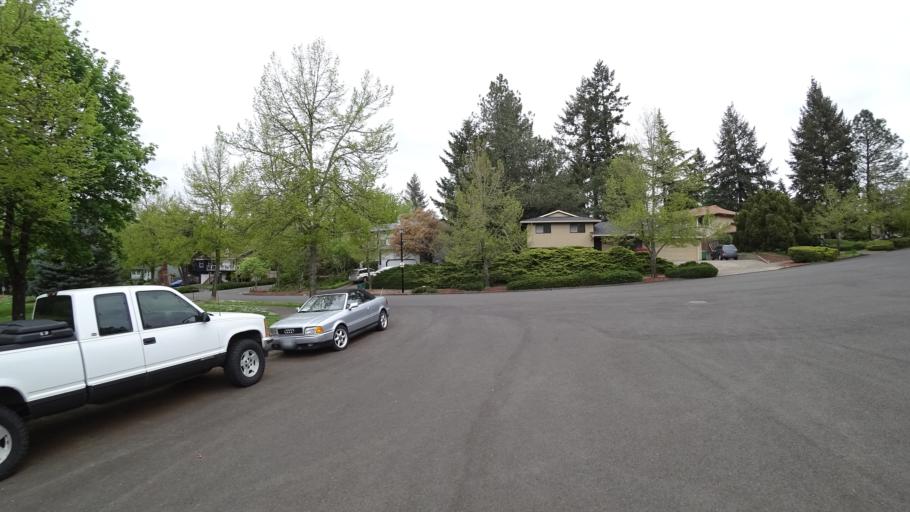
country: US
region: Oregon
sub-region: Washington County
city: Beaverton
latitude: 45.4625
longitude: -122.8292
